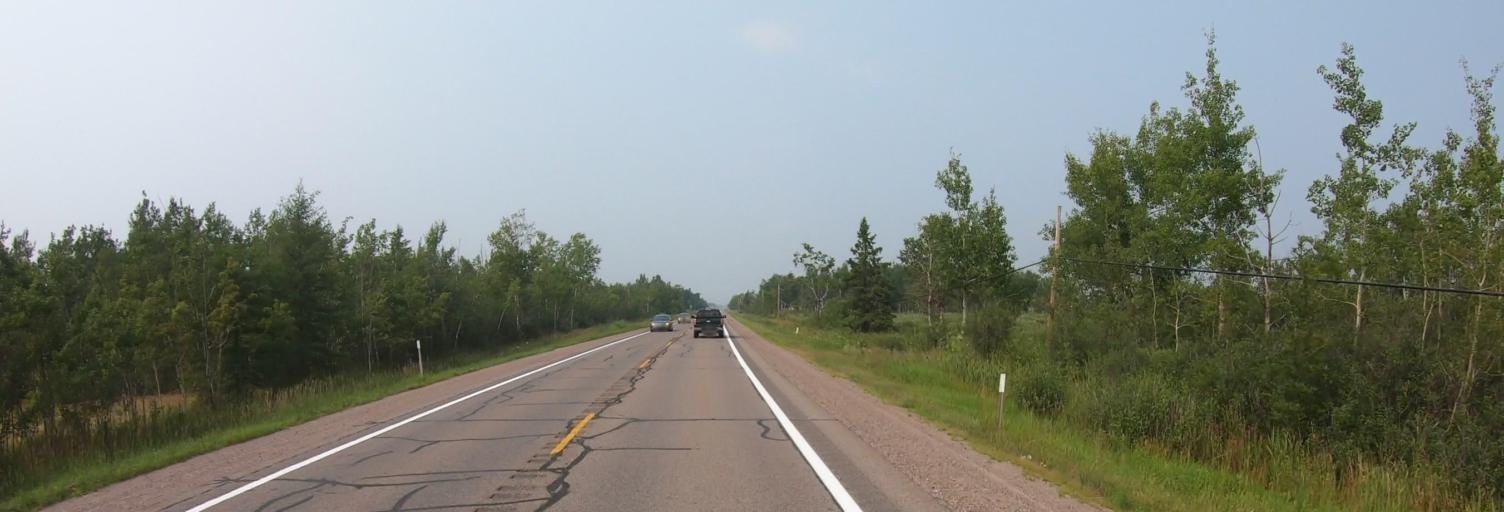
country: US
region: Michigan
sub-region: Chippewa County
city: Sault Ste. Marie
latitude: 46.4504
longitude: -84.3540
